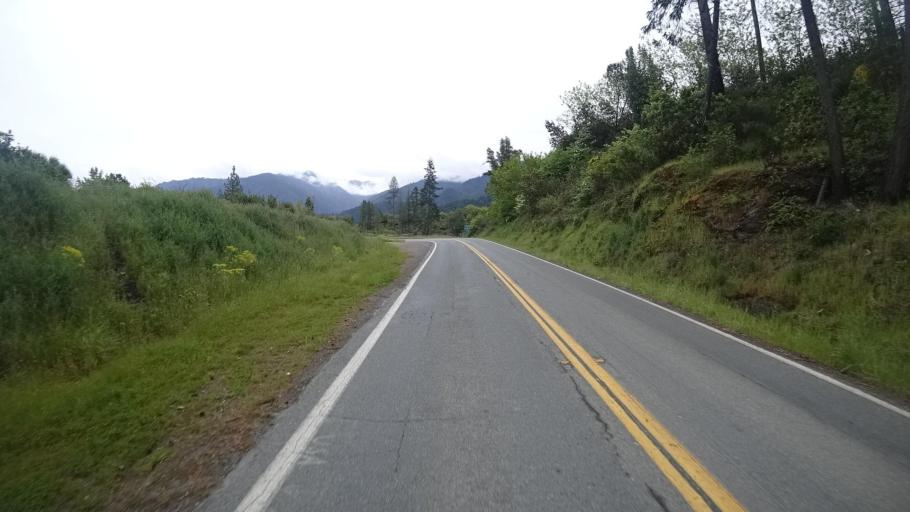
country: US
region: California
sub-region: Humboldt County
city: Willow Creek
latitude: 41.2968
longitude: -123.5548
